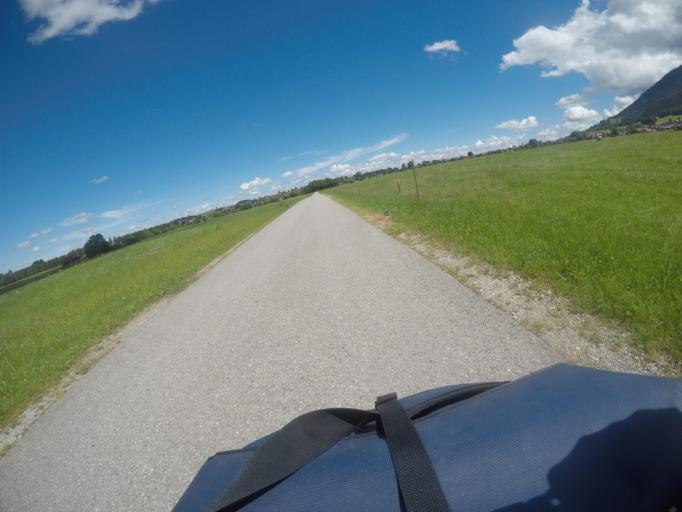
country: DE
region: Bavaria
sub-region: Swabia
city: Halblech
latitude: 47.6146
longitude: 10.7986
